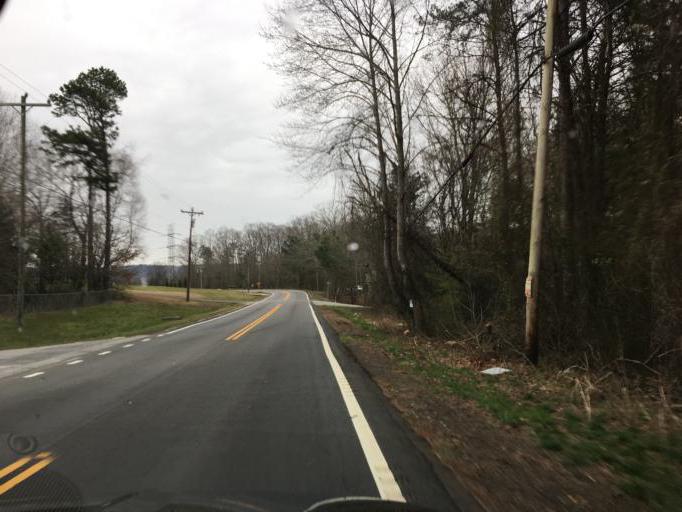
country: US
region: South Carolina
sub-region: Greenville County
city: Berea
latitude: 34.9177
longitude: -82.4723
